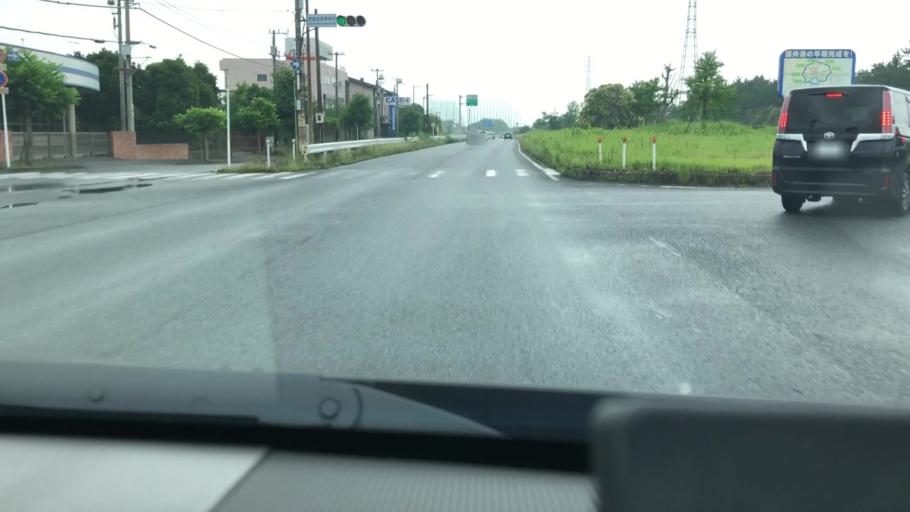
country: JP
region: Chiba
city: Kisarazu
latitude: 35.4447
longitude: 139.9768
